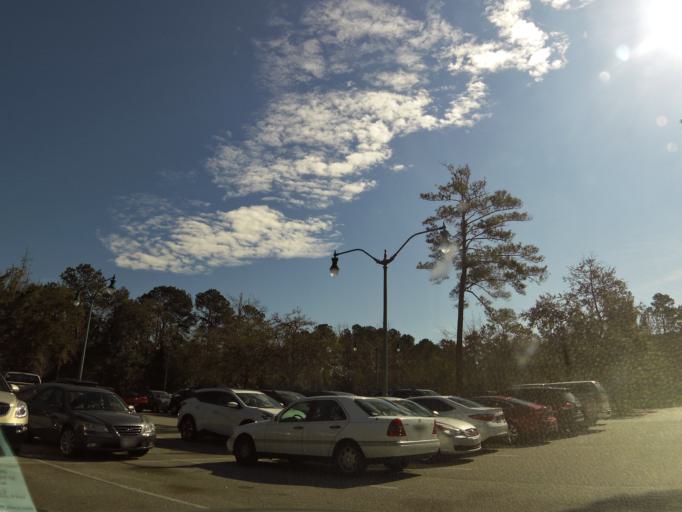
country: US
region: South Carolina
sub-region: Charleston County
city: Isle of Palms
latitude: 32.8239
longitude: -79.8178
